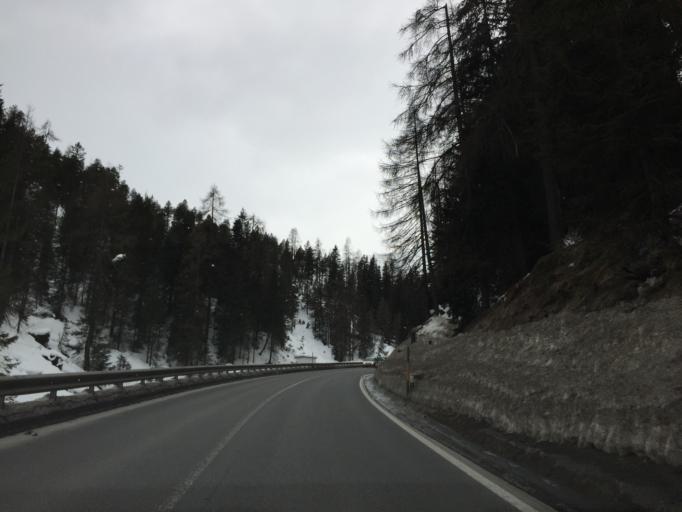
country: CH
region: Grisons
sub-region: Praettigau/Davos District
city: Davos
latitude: 46.8405
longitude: 9.8638
